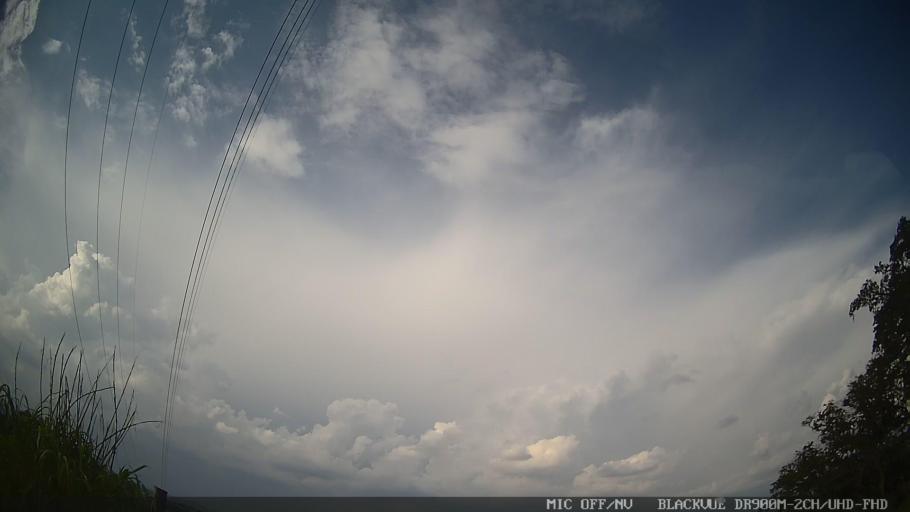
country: BR
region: Sao Paulo
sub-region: Braganca Paulista
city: Braganca Paulista
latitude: -22.9176
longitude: -46.5682
